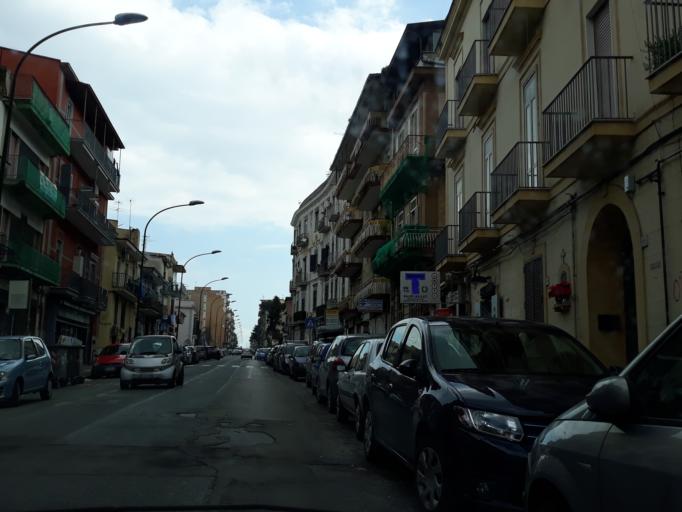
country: IT
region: Campania
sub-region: Provincia di Napoli
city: Mugnano di Napoli
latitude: 40.8855
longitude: 14.2289
